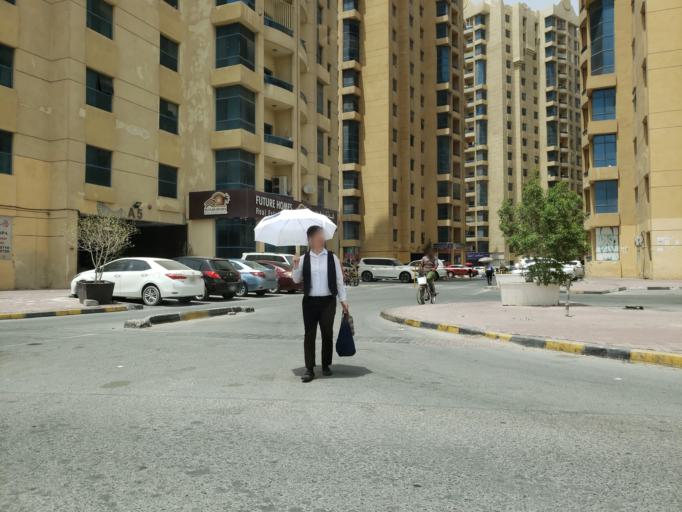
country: AE
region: Ajman
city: Ajman
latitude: 25.3936
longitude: 55.4565
